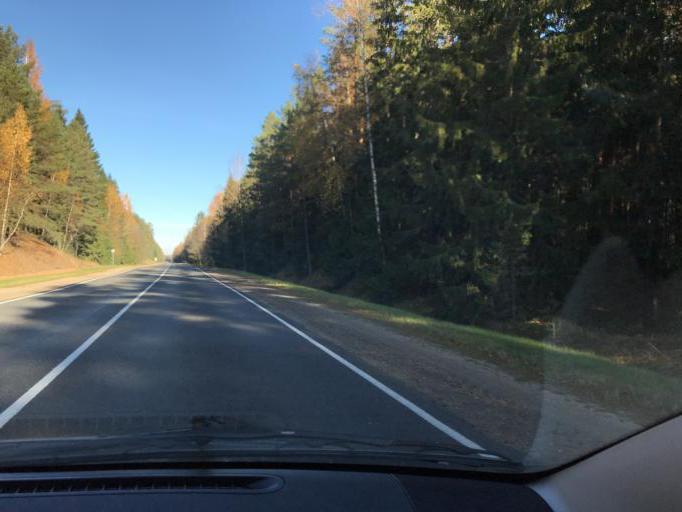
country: BY
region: Vitebsk
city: Polatsk
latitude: 55.3616
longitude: 28.8072
